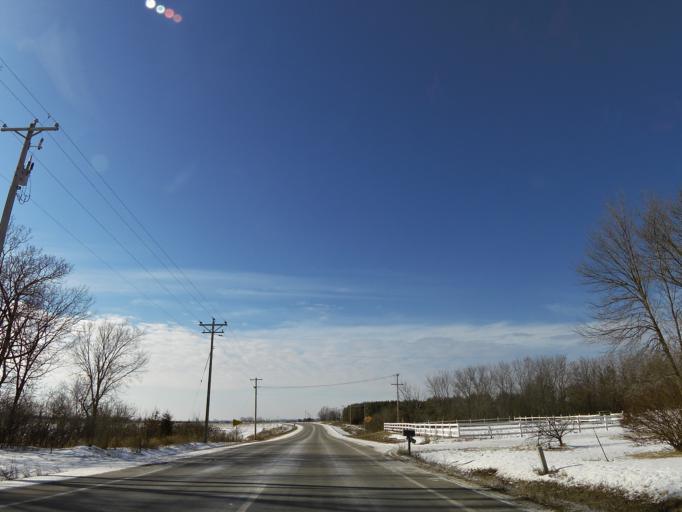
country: US
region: Wisconsin
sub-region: Saint Croix County
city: North Hudson
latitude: 44.9888
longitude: -92.6698
